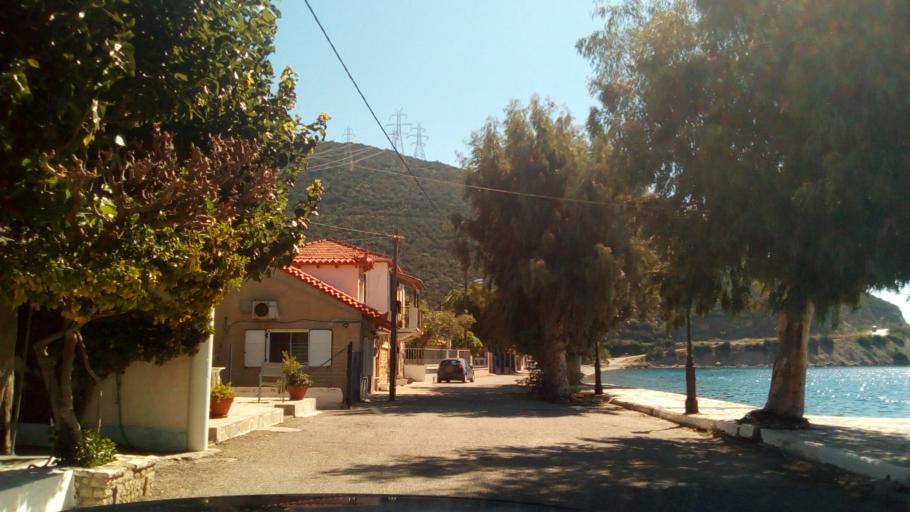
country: GR
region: West Greece
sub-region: Nomos Achaias
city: Aigio
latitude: 38.3664
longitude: 22.1270
